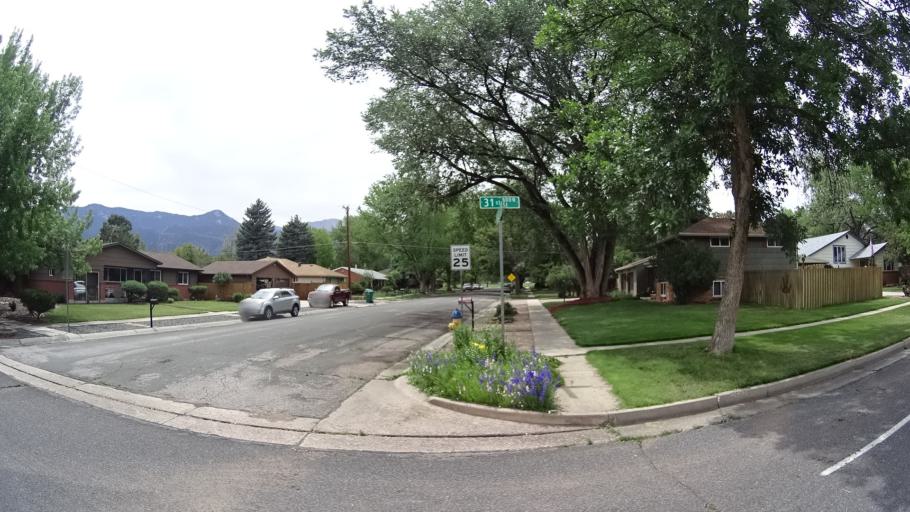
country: US
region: Colorado
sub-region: El Paso County
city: Manitou Springs
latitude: 38.8637
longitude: -104.8680
